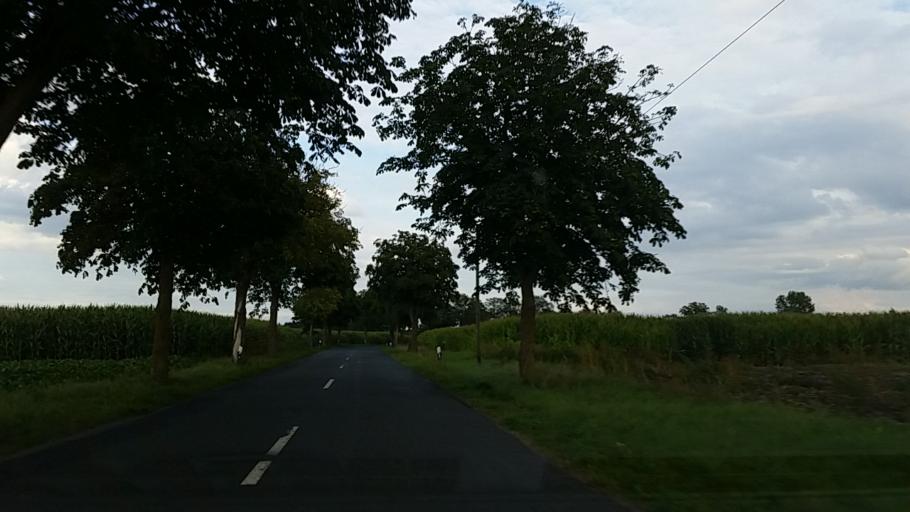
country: DE
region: Lower Saxony
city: Luder
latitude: 52.8120
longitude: 10.6544
